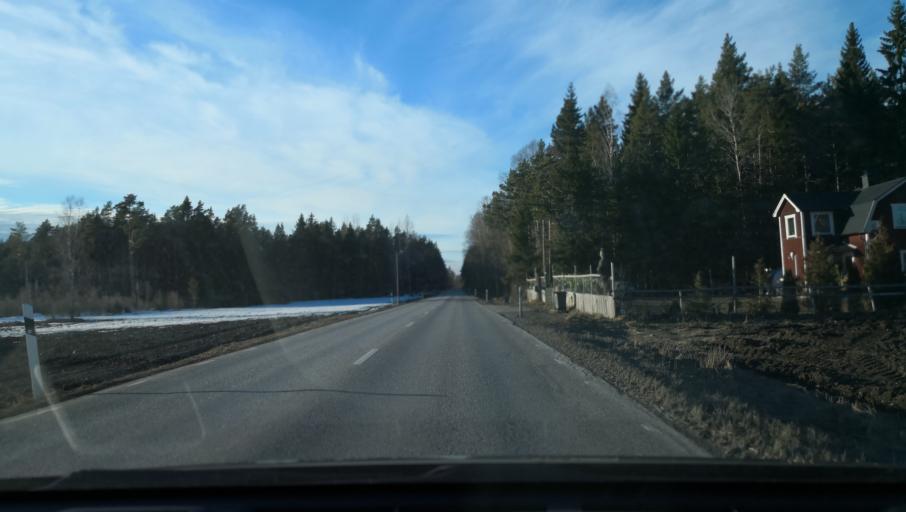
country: SE
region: Uppsala
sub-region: Osthammars Kommun
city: OEsthammar
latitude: 60.2711
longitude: 18.3178
